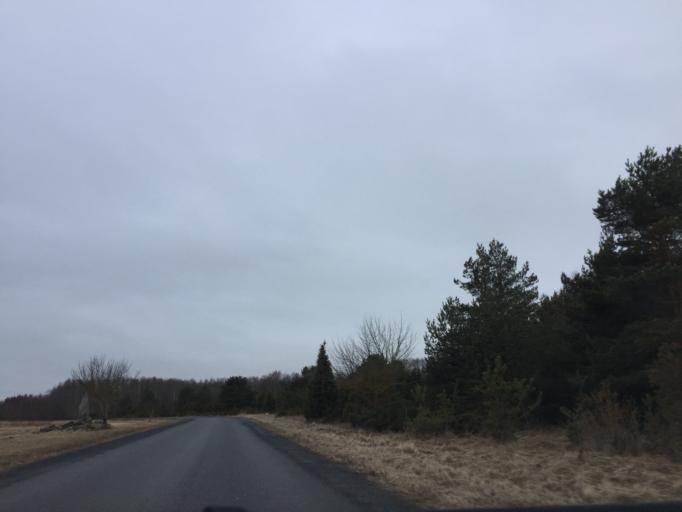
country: EE
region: Laeaene
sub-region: Haapsalu linn
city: Haapsalu
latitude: 58.7940
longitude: 23.4833
